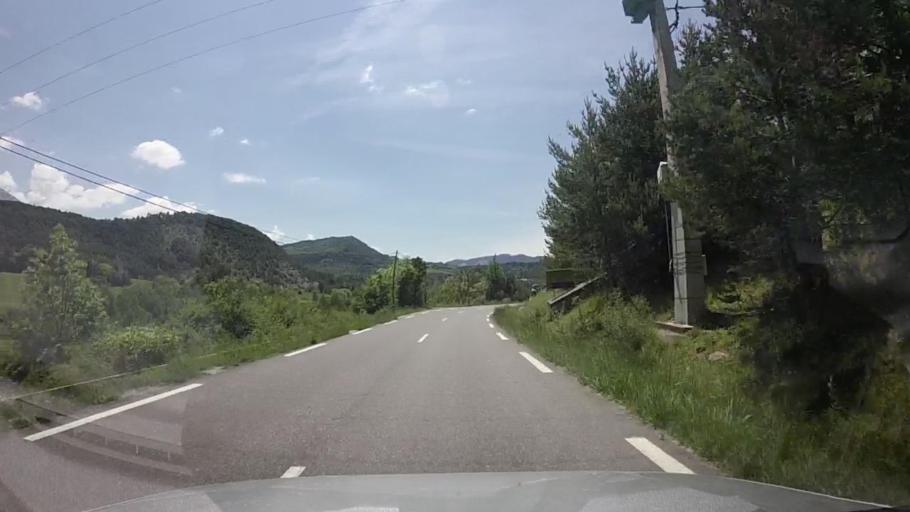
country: FR
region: Provence-Alpes-Cote d'Azur
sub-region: Departement des Alpes-de-Haute-Provence
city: Seyne-les-Alpes
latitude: 44.3878
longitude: 6.3289
